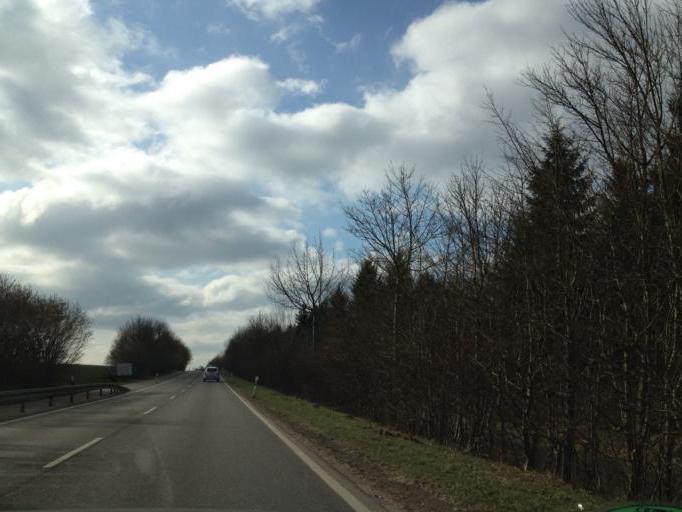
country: DE
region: Saarland
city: Sankt Wendel
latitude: 49.4693
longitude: 7.1333
